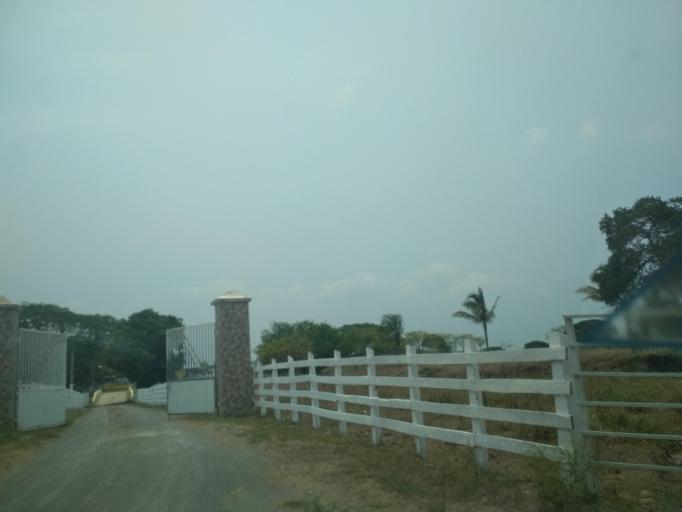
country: MX
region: Veracruz
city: Manlio Fabio Altamirano
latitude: 19.1364
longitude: -96.2907
